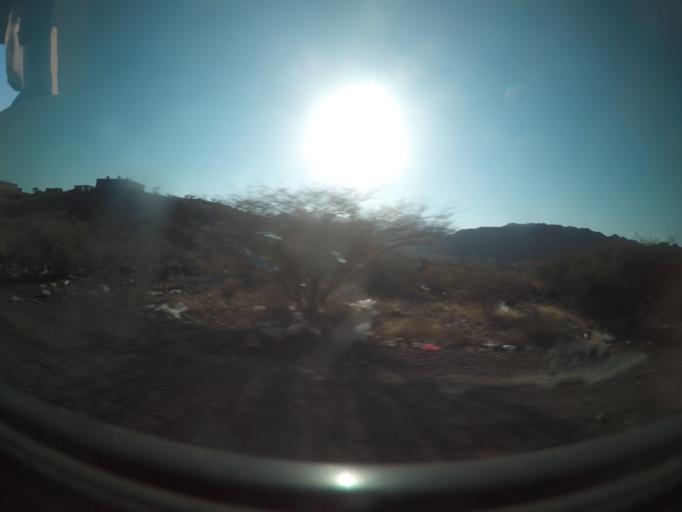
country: YE
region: Lahij
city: Habil ar Raydah
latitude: 13.6552
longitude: 44.8446
